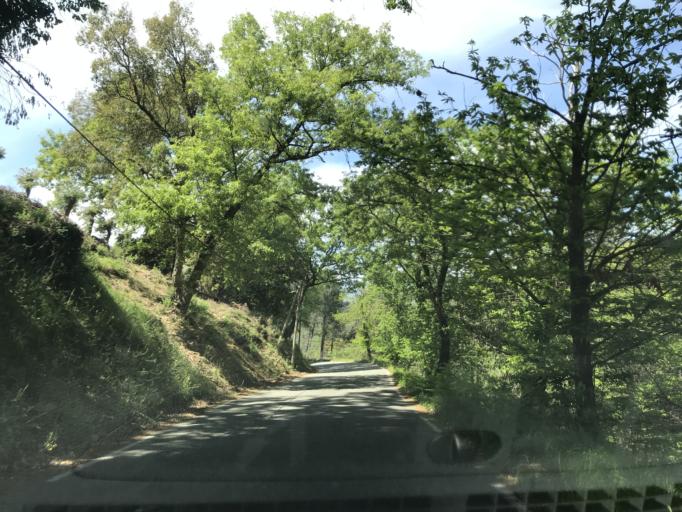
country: FR
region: Provence-Alpes-Cote d'Azur
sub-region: Departement du Var
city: Tanneron
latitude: 43.5822
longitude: 6.8314
